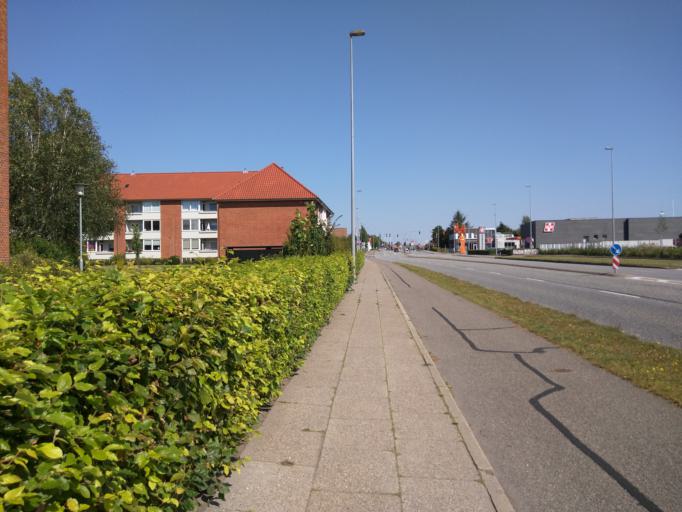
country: DK
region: Central Jutland
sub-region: Viborg Kommune
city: Viborg
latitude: 56.4530
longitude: 9.3923
